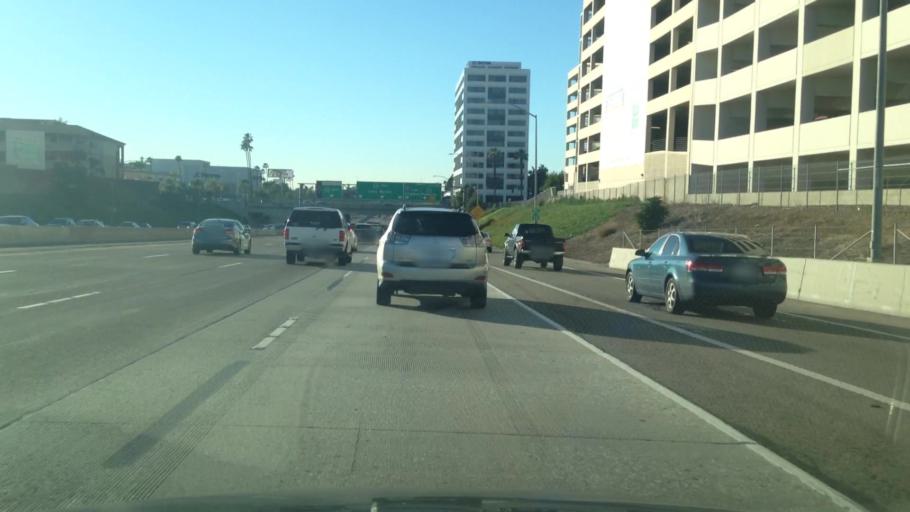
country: US
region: California
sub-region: Orange County
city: Orange
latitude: 33.7784
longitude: -117.8642
